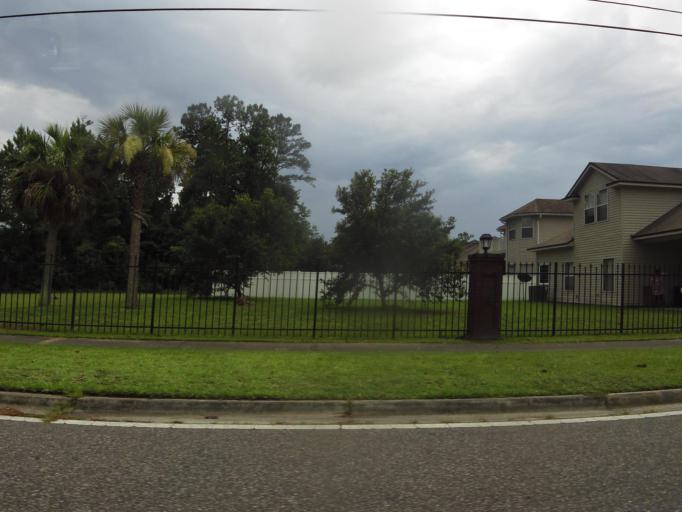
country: US
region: Florida
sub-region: Duval County
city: Jacksonville
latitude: 30.4274
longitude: -81.7175
